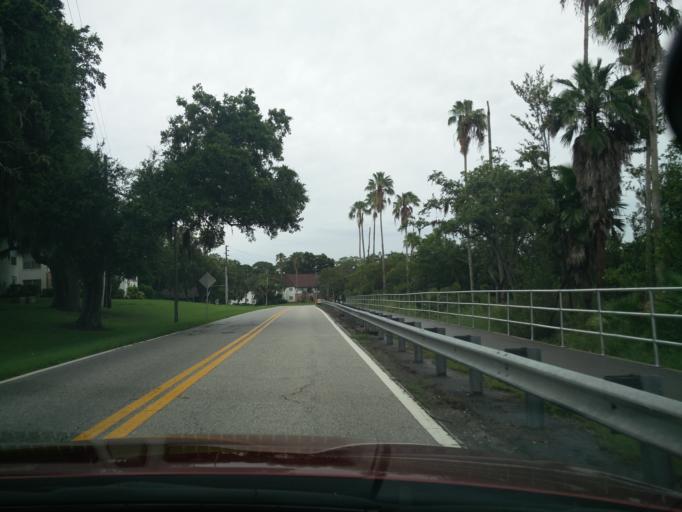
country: US
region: Florida
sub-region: Pinellas County
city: Safety Harbor
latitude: 27.9687
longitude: -82.7030
